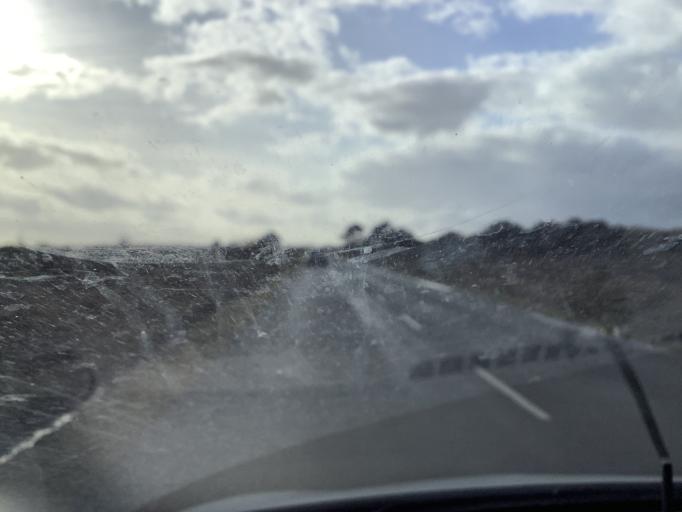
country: GB
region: England
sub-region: Hampshire
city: Lymington
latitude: 50.8136
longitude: -1.5007
